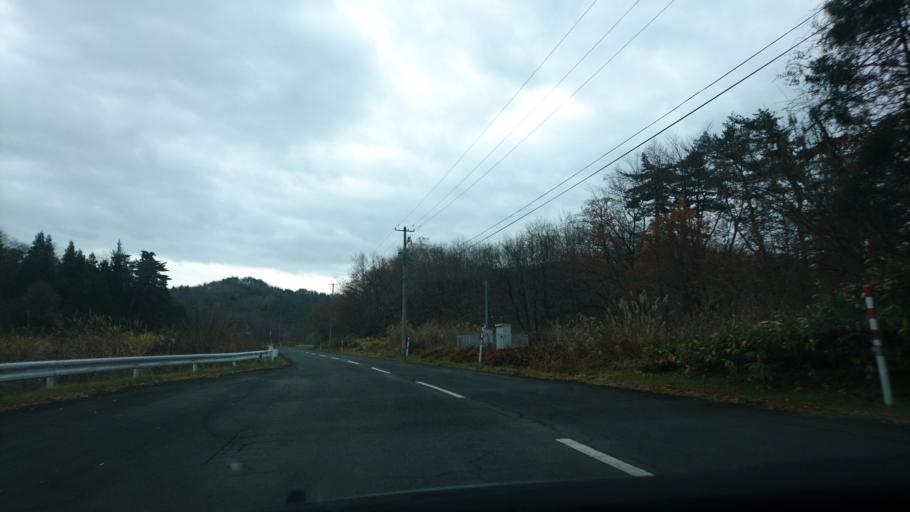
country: JP
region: Iwate
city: Ichinoseki
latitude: 38.9296
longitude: 140.9220
